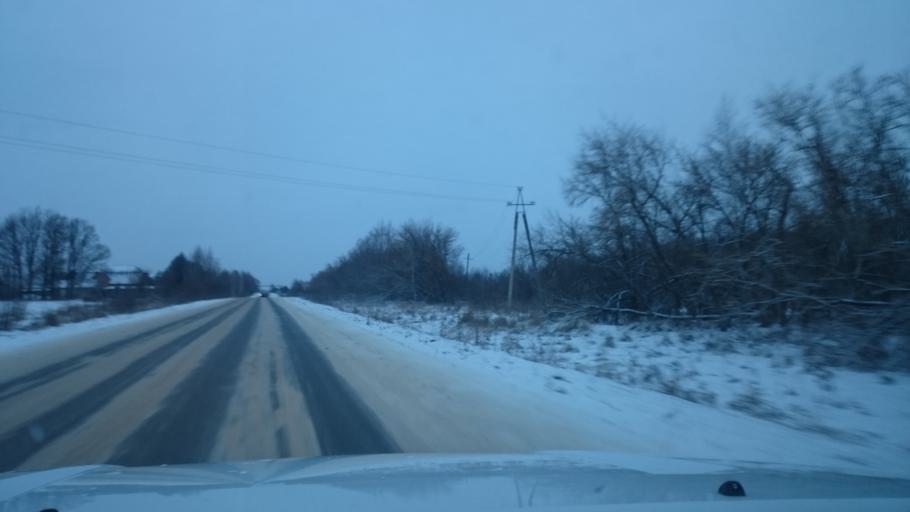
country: RU
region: Tula
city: Leninskiy
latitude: 54.2493
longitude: 37.3841
